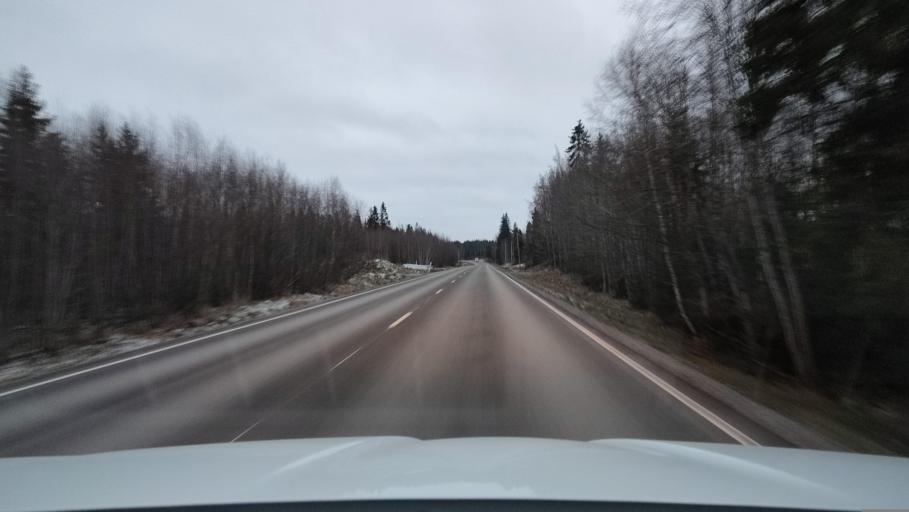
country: FI
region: Ostrobothnia
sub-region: Vaasa
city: Replot
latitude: 63.2151
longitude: 21.4278
